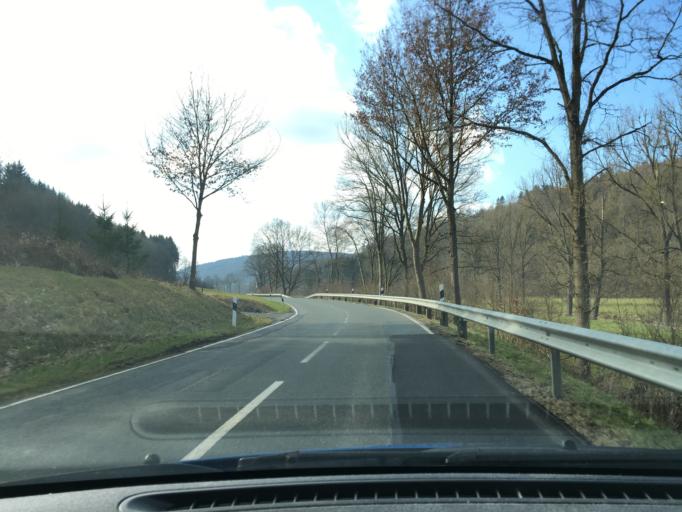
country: DE
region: Lower Saxony
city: Uslar
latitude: 51.6208
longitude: 9.6455
